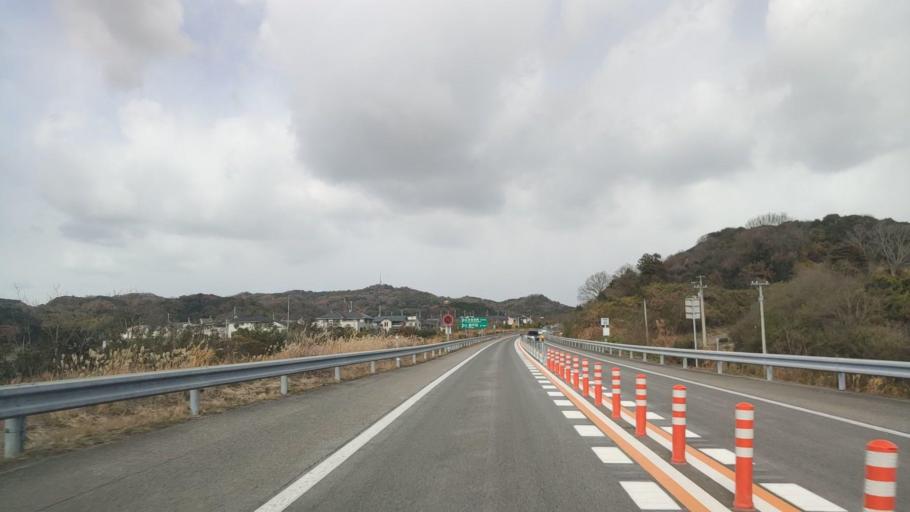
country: JP
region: Ehime
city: Hojo
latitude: 34.0652
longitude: 132.9733
